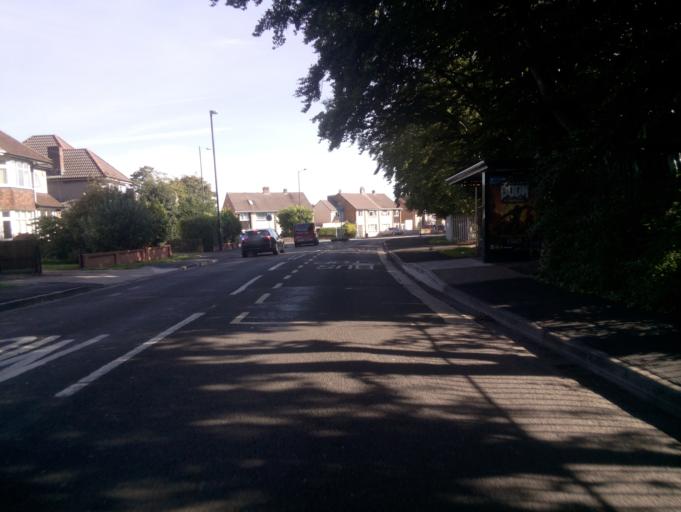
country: GB
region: England
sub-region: Bath and North East Somerset
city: Whitchurch
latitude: 51.4258
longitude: -2.5571
